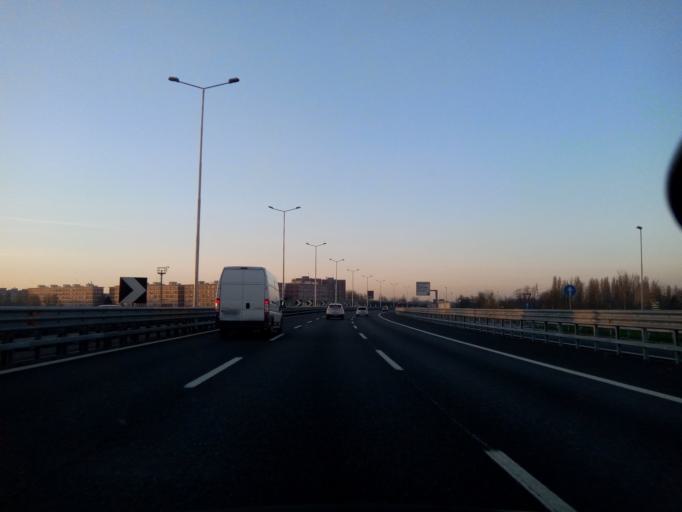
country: IT
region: Lombardy
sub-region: Citta metropolitana di Milano
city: Cesano Boscone
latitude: 45.4586
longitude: 9.0772
